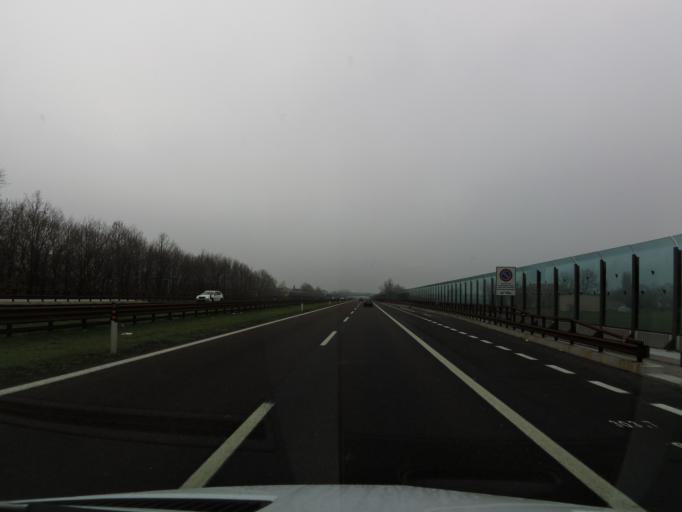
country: IT
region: Emilia-Romagna
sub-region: Provincia di Modena
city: Santa Croce Scuole
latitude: 44.7515
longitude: 10.8448
